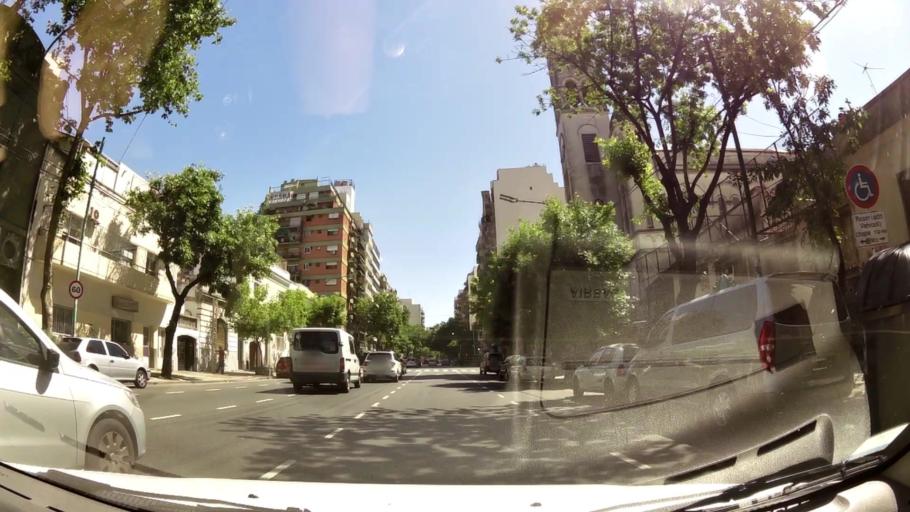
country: AR
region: Buenos Aires F.D.
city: Villa Santa Rita
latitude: -34.6235
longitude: -58.4445
